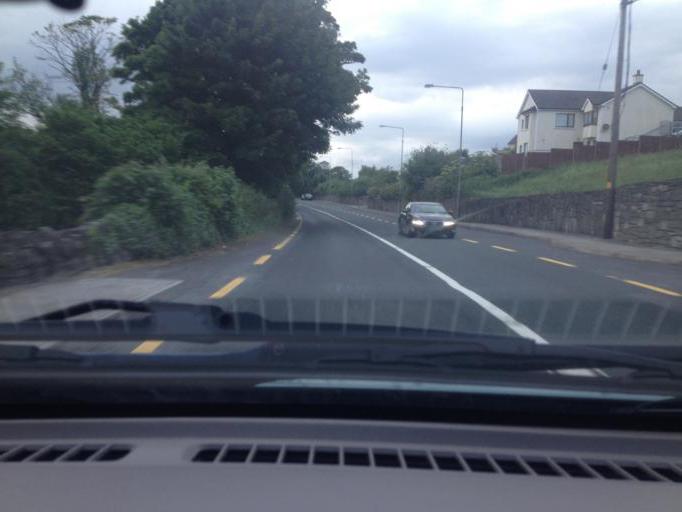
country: IE
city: Ballisodare
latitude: 54.2129
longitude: -8.5101
